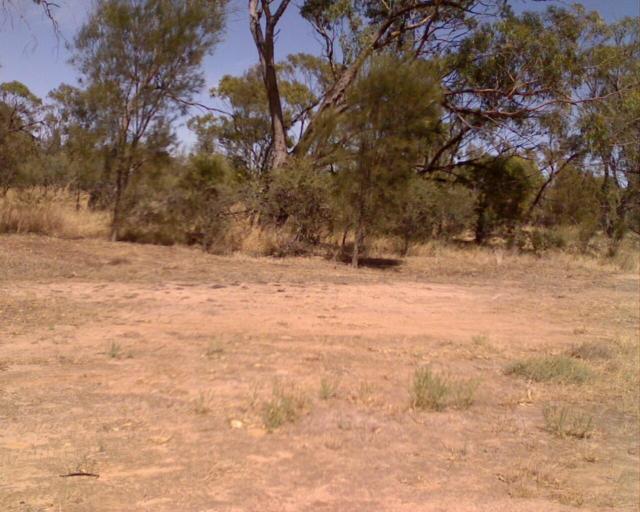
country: AU
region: Western Australia
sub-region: Moora
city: Moora
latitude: -30.2933
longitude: 116.0621
